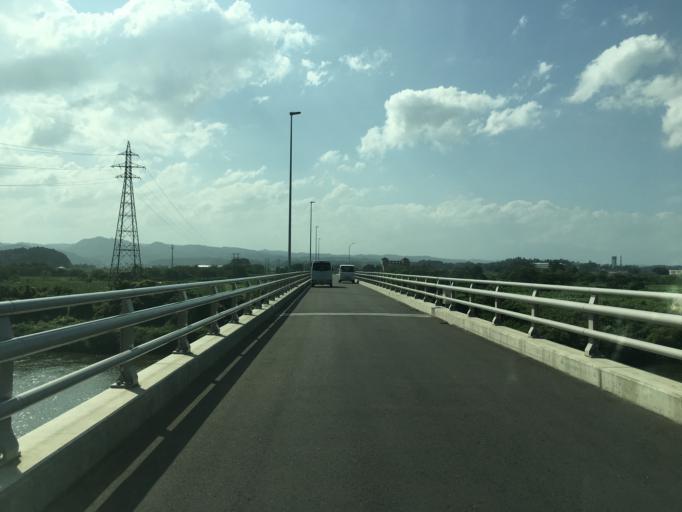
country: JP
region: Miyagi
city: Kakuda
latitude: 37.9592
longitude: 140.7915
